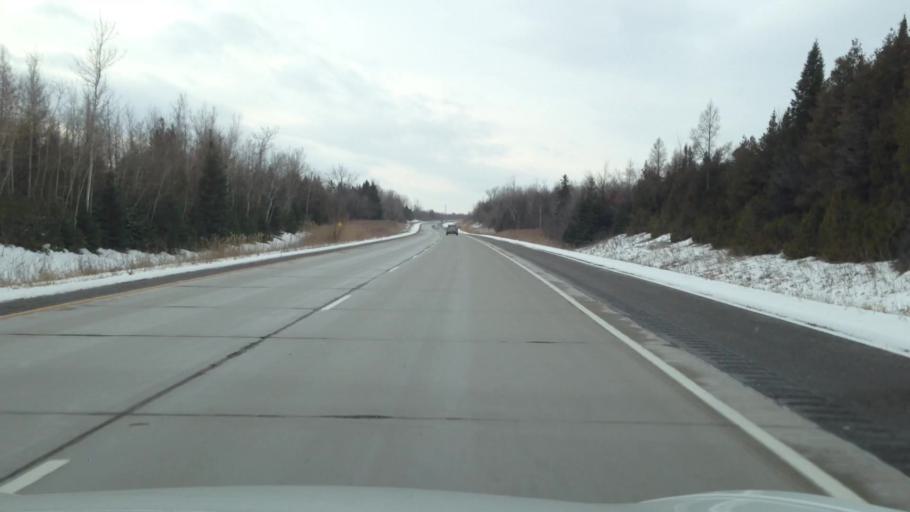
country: CA
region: Ontario
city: Hawkesbury
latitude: 45.4897
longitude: -74.6266
